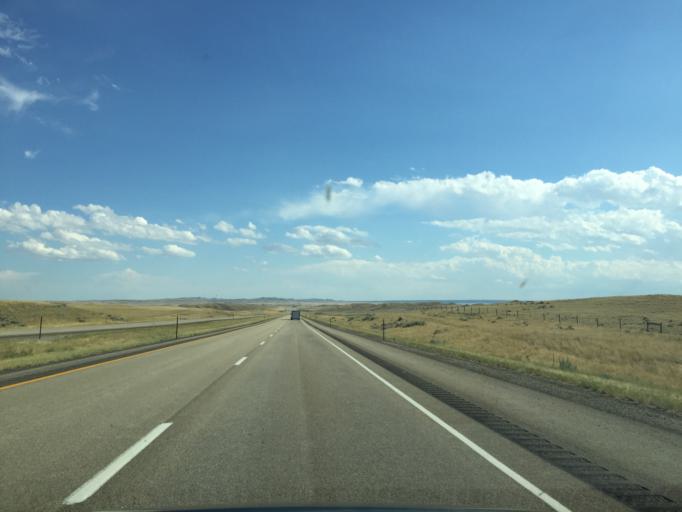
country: US
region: Wyoming
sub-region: Johnson County
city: Buffalo
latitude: 44.1125
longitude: -106.6371
